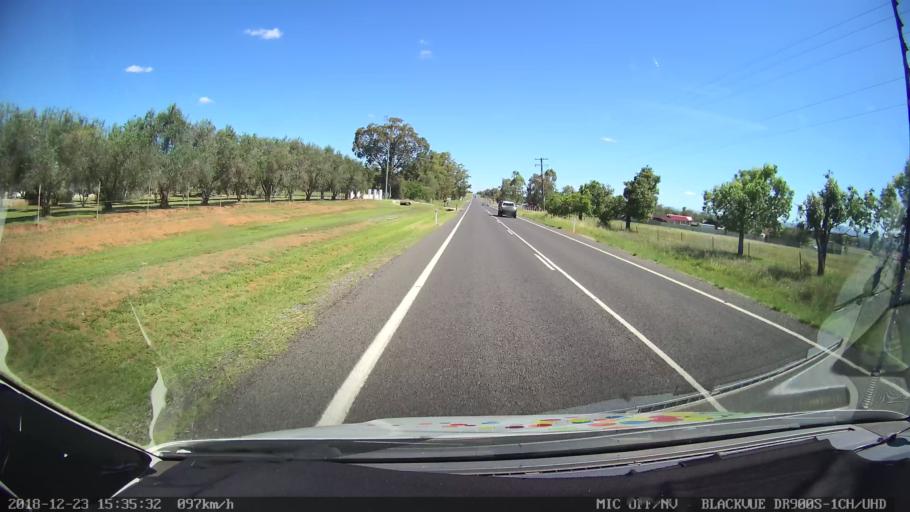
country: AU
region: New South Wales
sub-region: Tamworth Municipality
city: Tamworth
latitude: -31.0286
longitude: 150.8829
